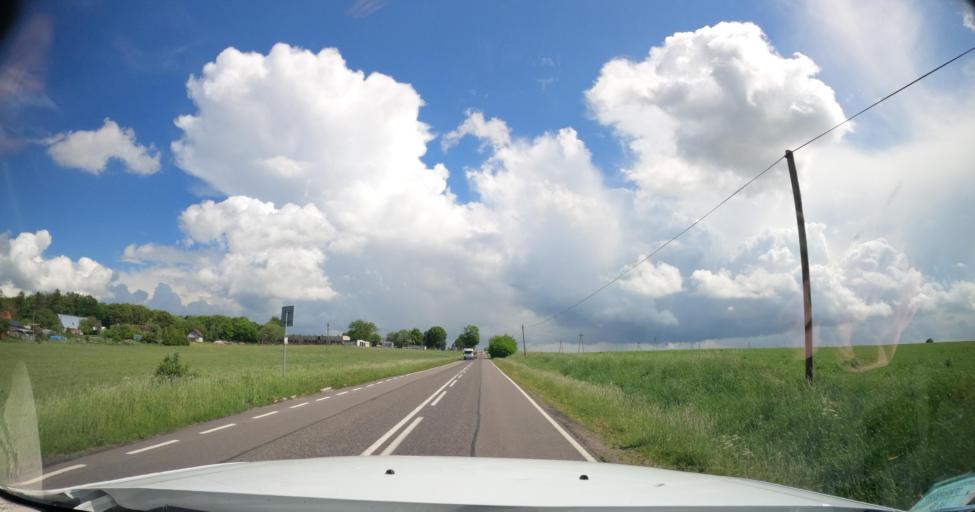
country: PL
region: Pomeranian Voivodeship
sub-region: Powiat bytowski
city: Czarna Dabrowka
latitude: 54.3662
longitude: 17.5069
